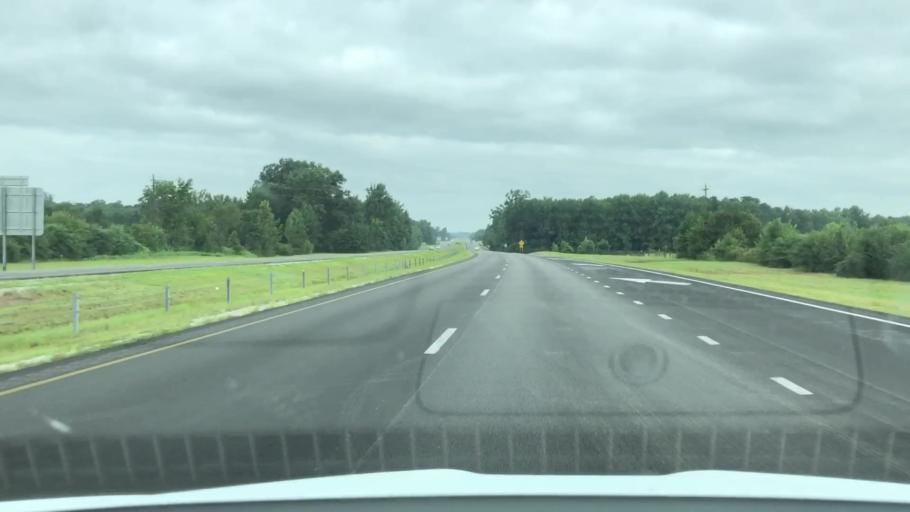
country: US
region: North Carolina
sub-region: Wayne County
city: Fremont
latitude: 35.5542
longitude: -77.9868
